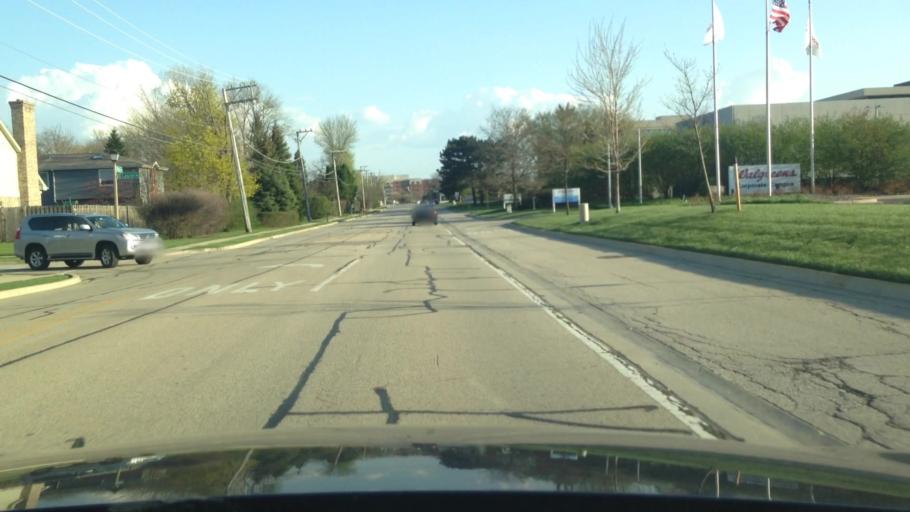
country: US
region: Illinois
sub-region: Lake County
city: Deerfield
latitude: 42.1569
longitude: -87.8674
